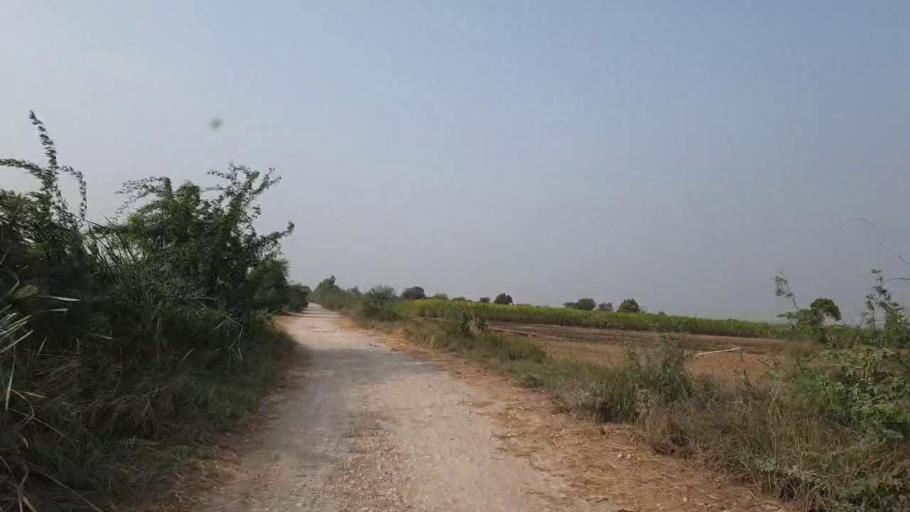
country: PK
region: Sindh
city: Tando Muhammad Khan
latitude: 25.0835
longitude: 68.5860
